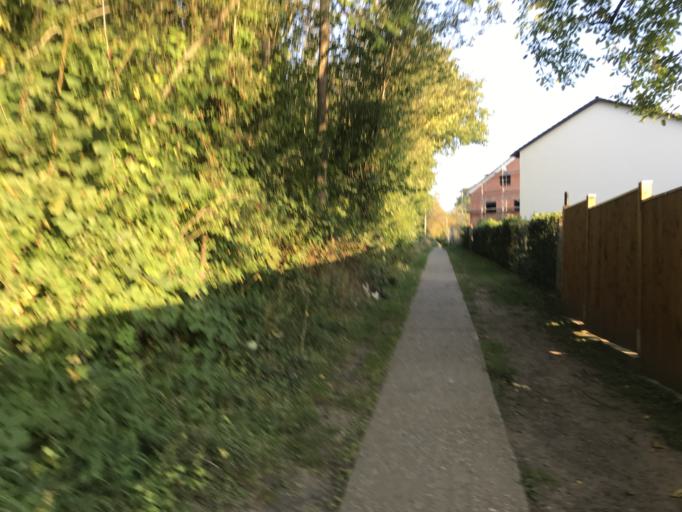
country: DE
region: Hesse
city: Nidderau
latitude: 50.2362
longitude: 8.8744
